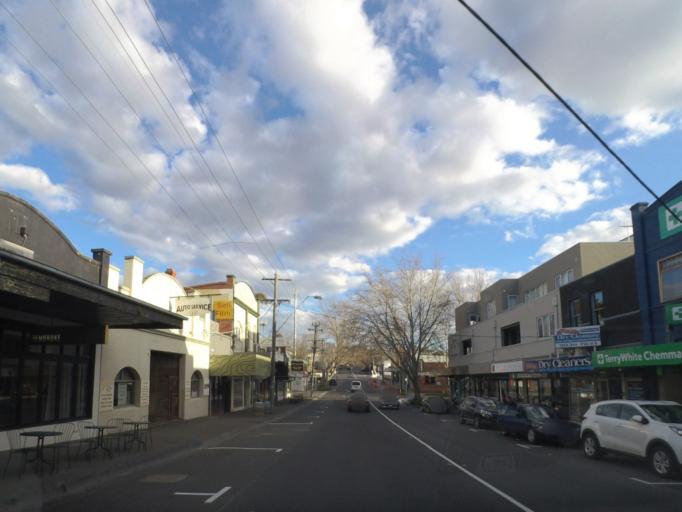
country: AU
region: Victoria
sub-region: Whitehorse
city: Surrey Hills
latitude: -37.8233
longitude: 145.0978
